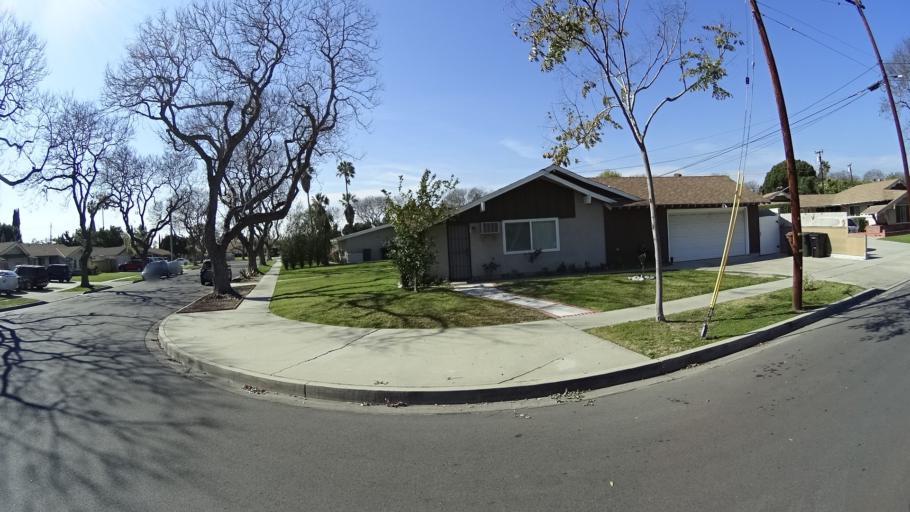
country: US
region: California
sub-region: Orange County
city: Garden Grove
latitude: 33.8001
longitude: -117.9354
